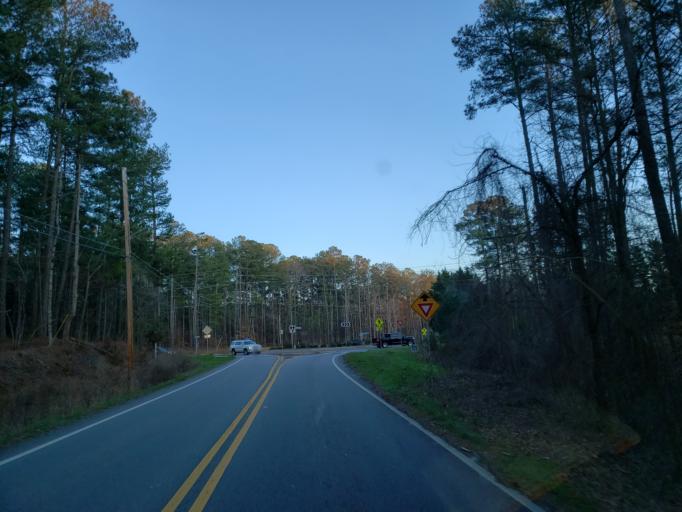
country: US
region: Georgia
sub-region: Cobb County
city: Acworth
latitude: 33.9985
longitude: -84.7299
